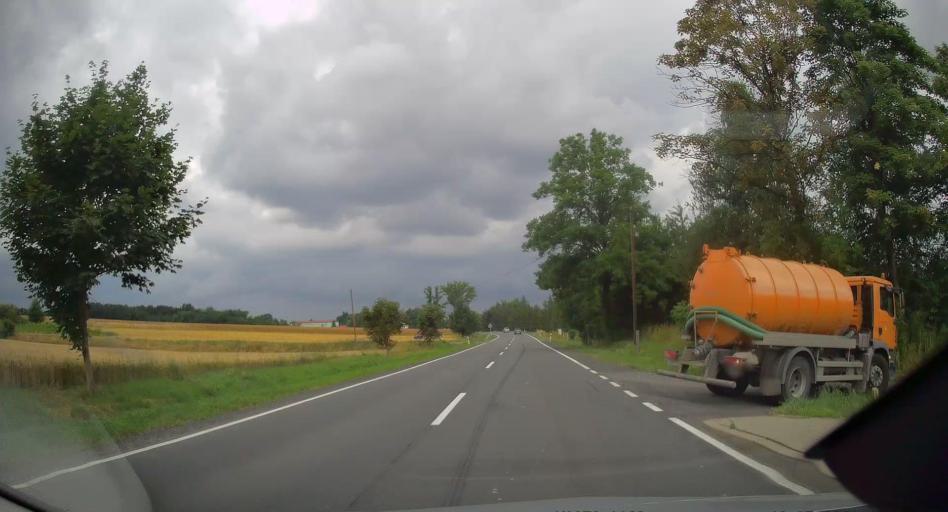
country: PL
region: Opole Voivodeship
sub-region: Powiat prudnicki
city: Laka Prudnicka
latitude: 50.3768
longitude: 17.5334
